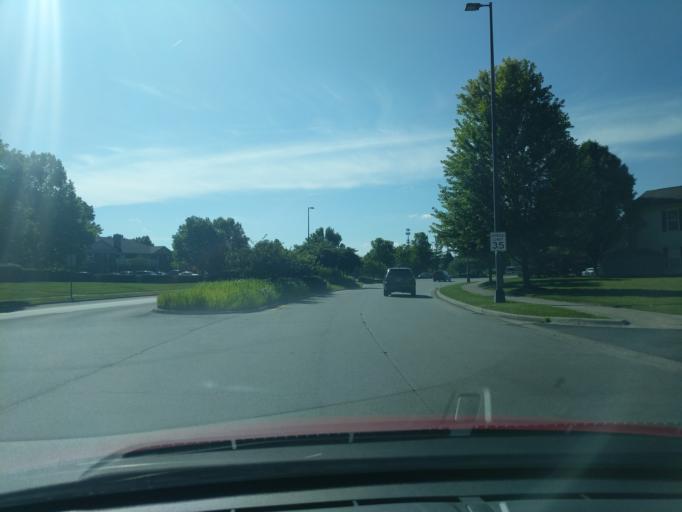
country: US
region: Ohio
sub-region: Franklin County
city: Huber Ridge
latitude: 40.0625
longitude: -82.9113
